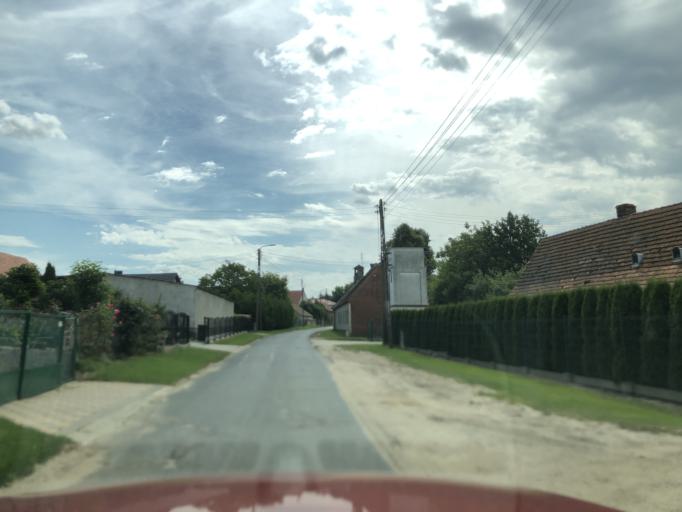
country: PL
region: Lower Silesian Voivodeship
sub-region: Powiat trzebnicki
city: Trzebnica
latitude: 51.3240
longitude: 17.0245
